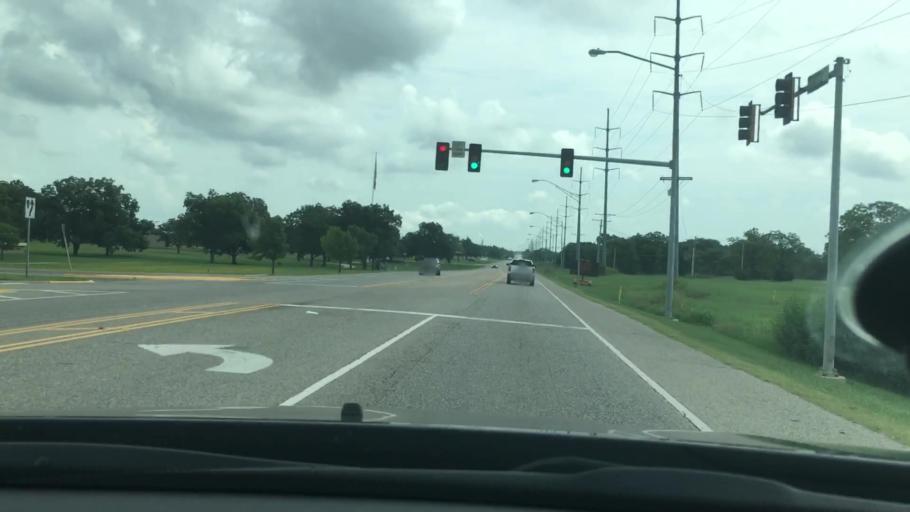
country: US
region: Oklahoma
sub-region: Carter County
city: Ardmore
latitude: 34.2028
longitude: -97.1354
